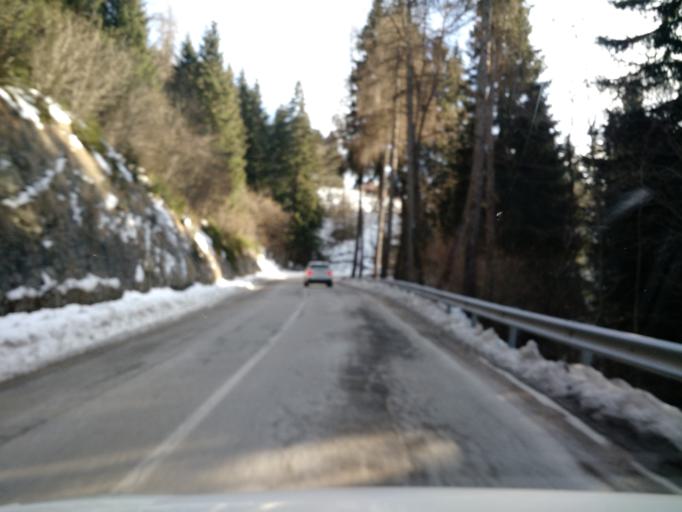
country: IT
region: Veneto
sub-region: Provincia di Vicenza
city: Canove di Roana
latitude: 45.8734
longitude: 11.4778
